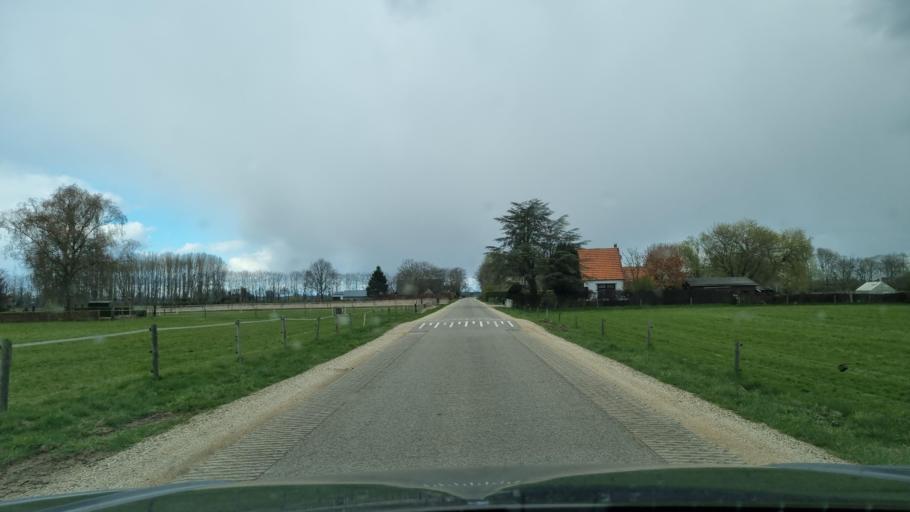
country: NL
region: Gelderland
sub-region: Gemeente Montferland
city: s-Heerenberg
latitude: 51.9050
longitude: 6.1777
